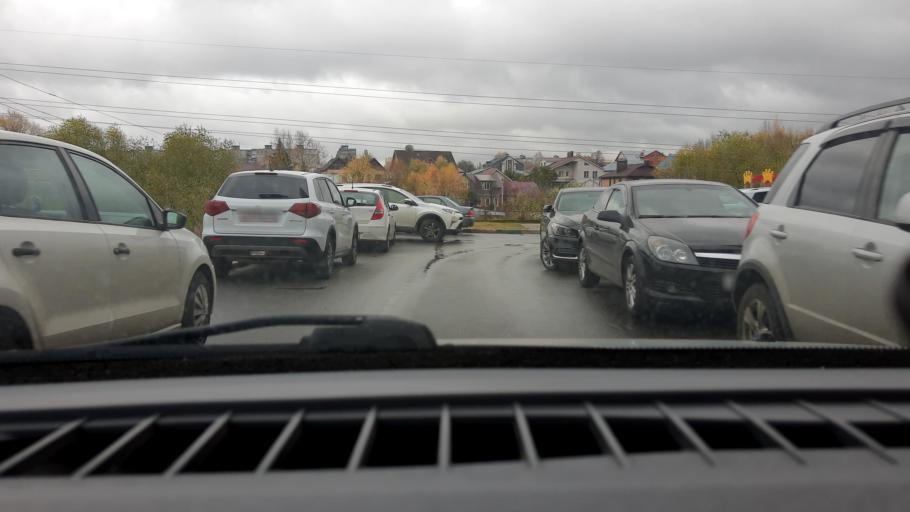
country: RU
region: Nizjnij Novgorod
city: Nizhniy Novgorod
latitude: 56.3077
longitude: 44.0330
